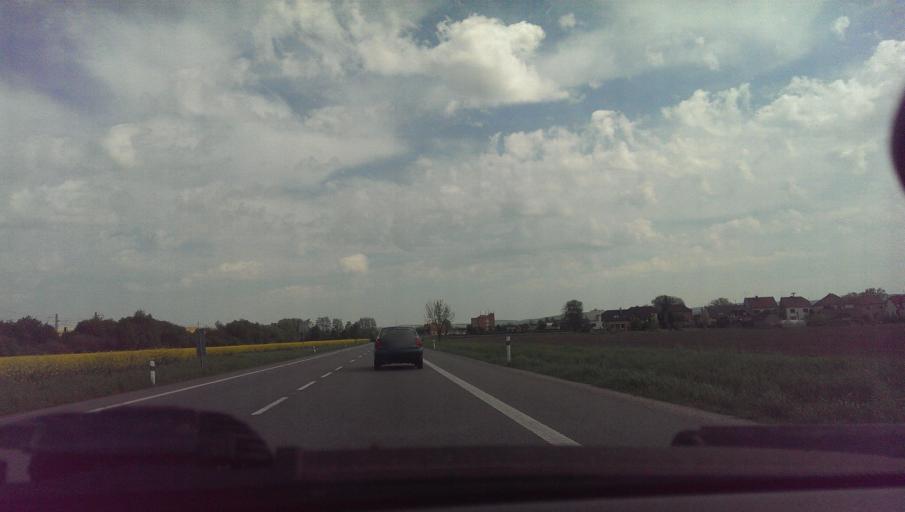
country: CZ
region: Zlin
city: Babice
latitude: 49.1250
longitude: 17.4778
